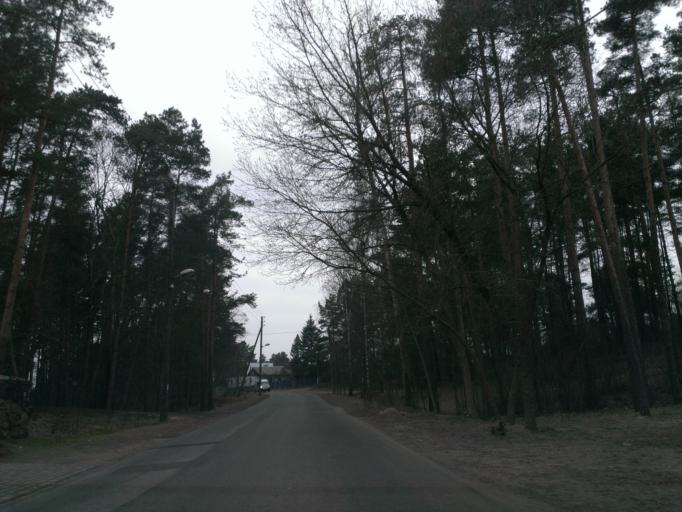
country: LV
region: Riga
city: Bergi
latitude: 56.9845
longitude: 24.2991
